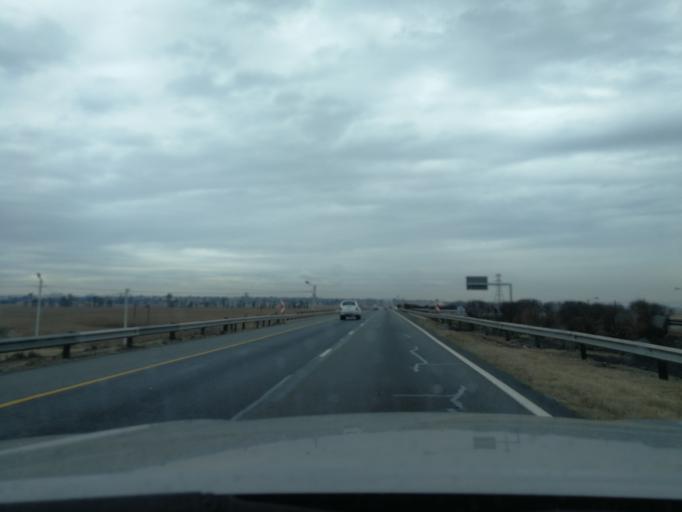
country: ZA
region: Gauteng
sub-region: Ekurhuleni Metropolitan Municipality
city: Germiston
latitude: -26.2968
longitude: 28.1594
